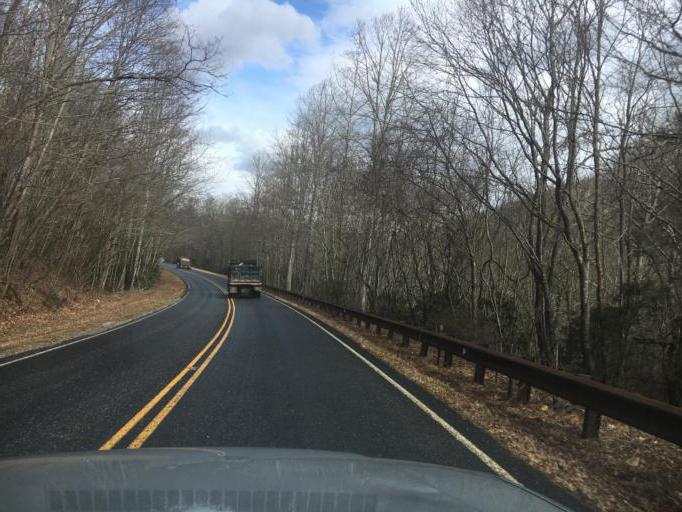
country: US
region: North Carolina
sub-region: Transylvania County
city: Brevard
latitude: 35.3670
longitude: -82.8171
